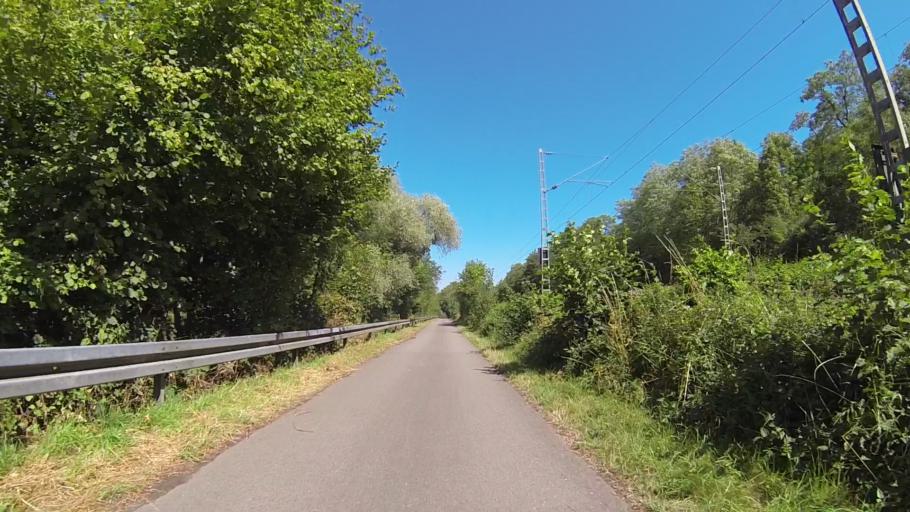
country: LU
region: Grevenmacher
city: Schengen
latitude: 49.4893
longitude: 6.3702
